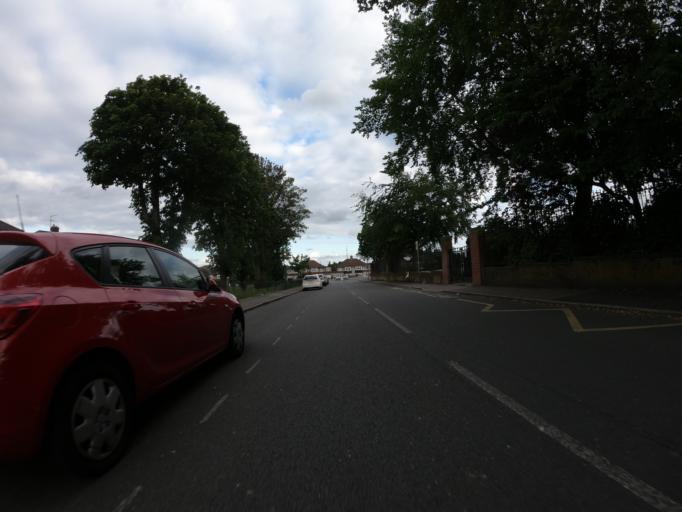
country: GB
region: England
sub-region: Greater London
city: Bexleyheath
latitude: 51.4787
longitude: 0.1356
